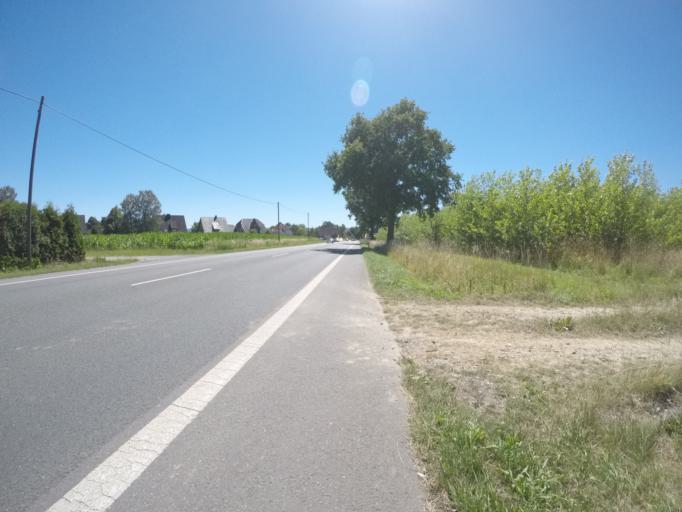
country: DE
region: North Rhine-Westphalia
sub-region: Regierungsbezirk Detmold
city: Bielefeld
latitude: 52.0765
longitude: 8.5823
